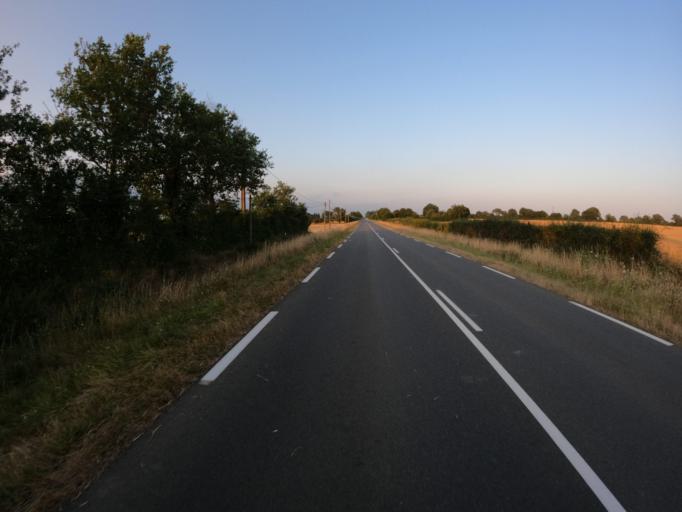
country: FR
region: Pays de la Loire
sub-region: Departement de la Mayenne
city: Meslay-du-Maine
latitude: 47.8614
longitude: -0.5767
